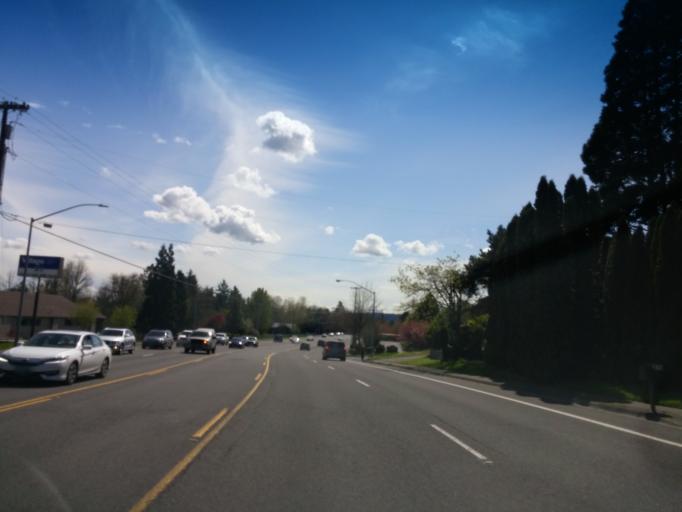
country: US
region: Oregon
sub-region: Washington County
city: Cedar Mill
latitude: 45.5170
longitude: -122.8176
